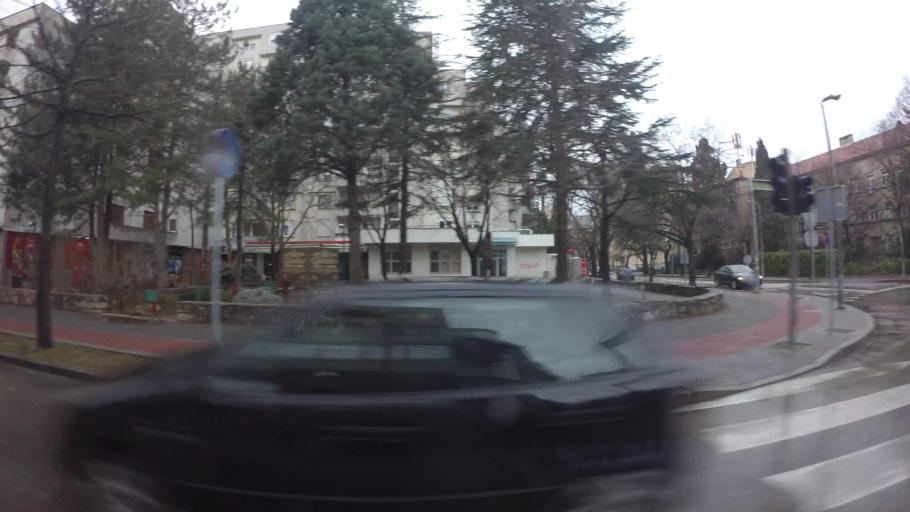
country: BA
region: Federation of Bosnia and Herzegovina
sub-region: Hercegovacko-Bosanski Kanton
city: Mostar
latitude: 43.3444
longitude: 17.8037
